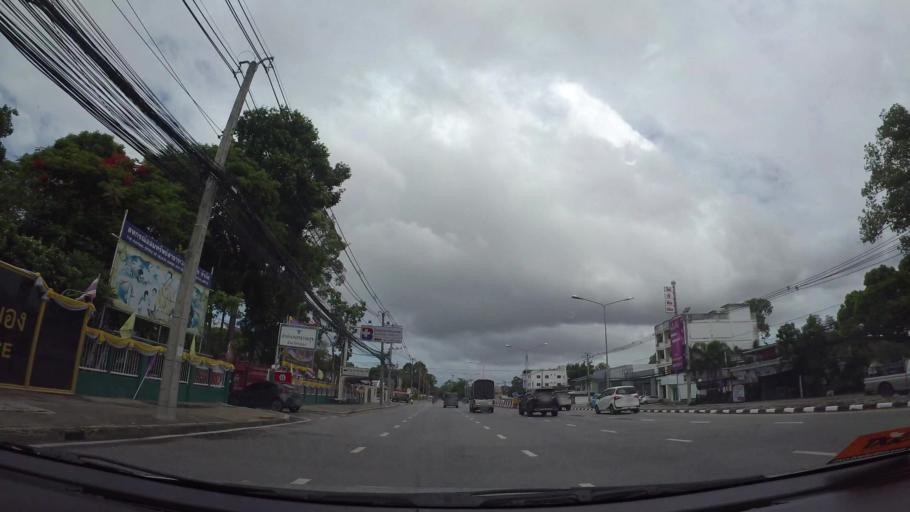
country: TH
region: Rayong
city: Rayong
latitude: 12.6835
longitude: 101.2226
